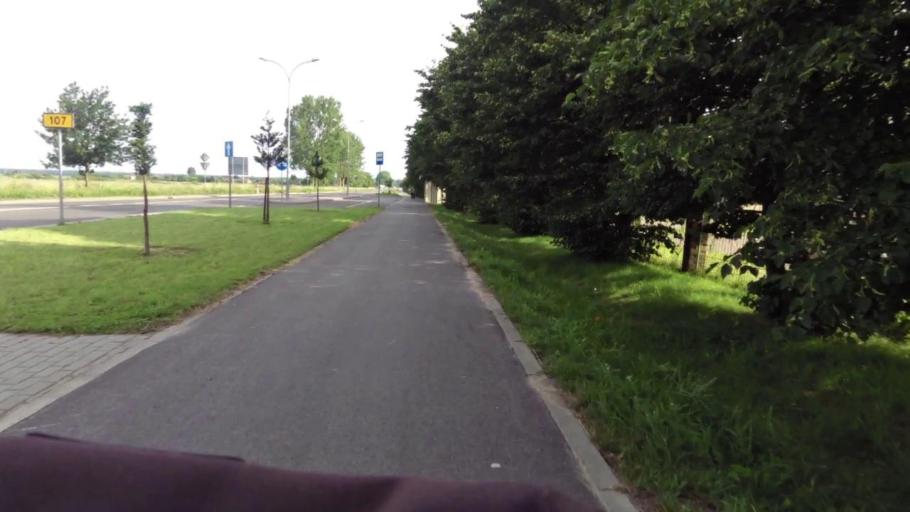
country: PL
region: West Pomeranian Voivodeship
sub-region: Powiat kamienski
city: Dziwnow
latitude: 54.0162
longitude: 14.8118
